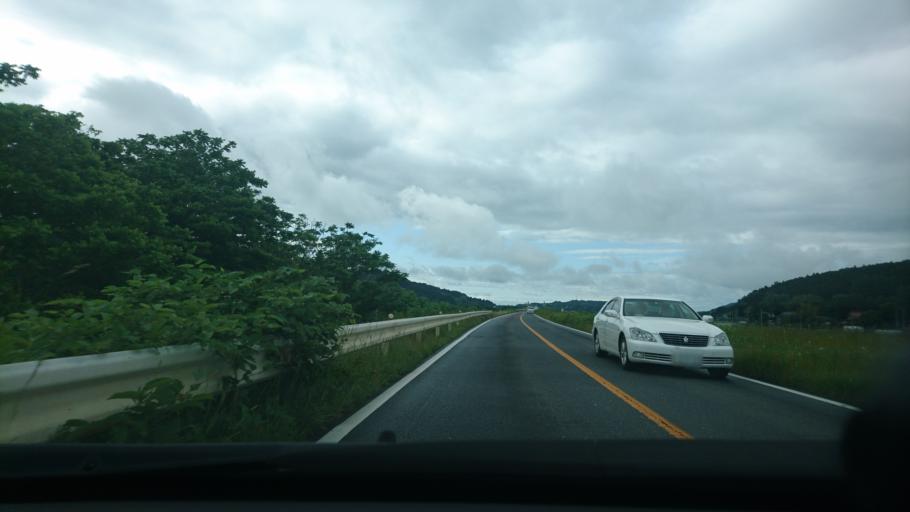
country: JP
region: Miyagi
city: Wakuya
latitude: 38.6316
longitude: 141.2909
